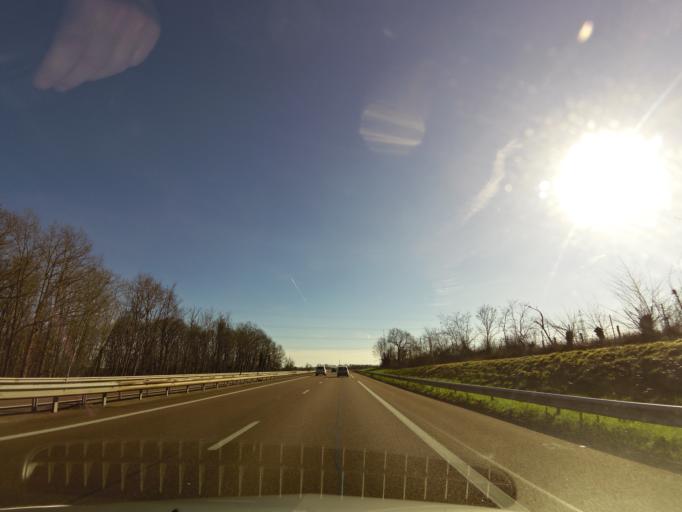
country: FR
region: Bourgogne
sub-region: Departement de l'Yonne
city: Venoy
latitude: 47.8110
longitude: 3.6273
